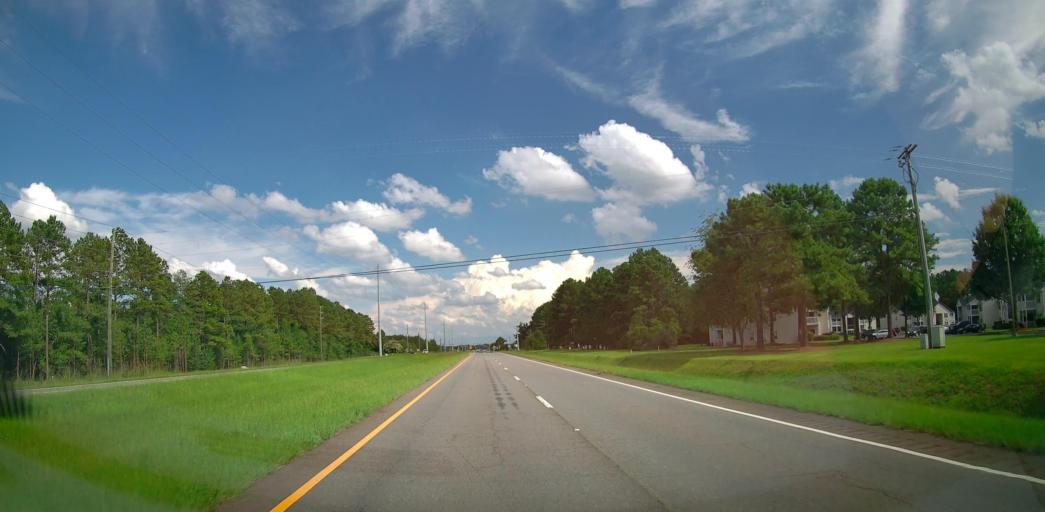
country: US
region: Georgia
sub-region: Houston County
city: Perry
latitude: 32.4793
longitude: -83.7096
